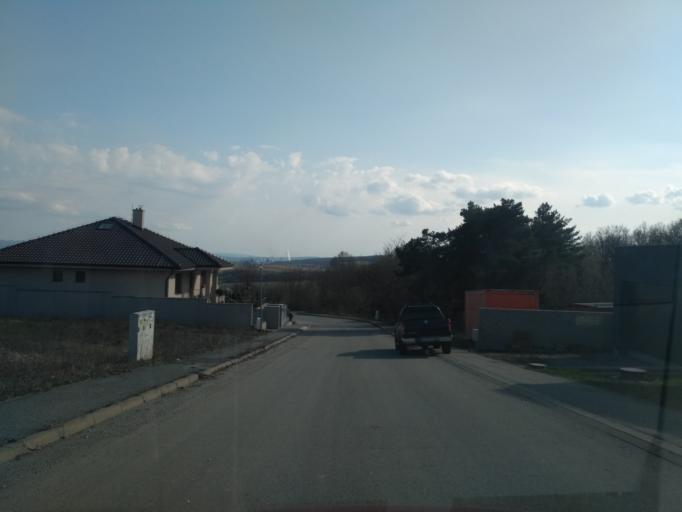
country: SK
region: Kosicky
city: Kosice
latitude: 48.6943
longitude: 21.1948
